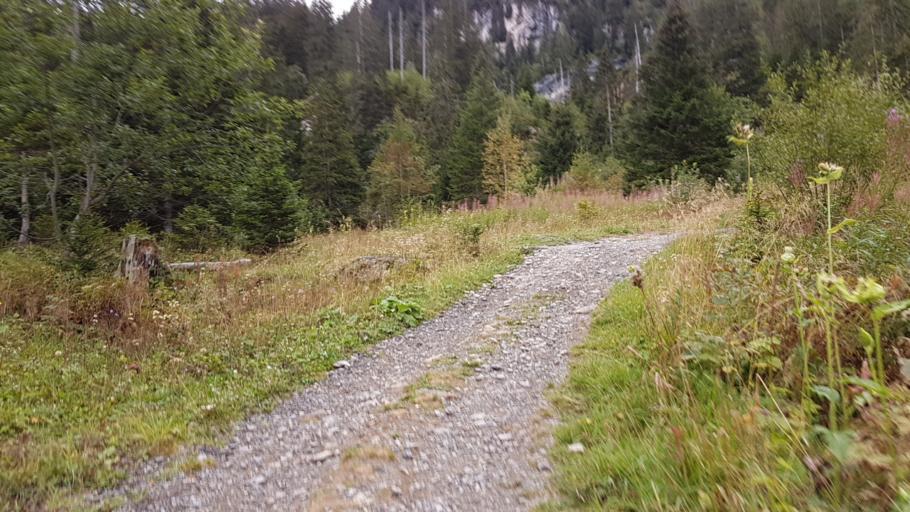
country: CH
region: Bern
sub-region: Frutigen-Niedersimmental District
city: Kandersteg
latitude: 46.4702
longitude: 7.6556
